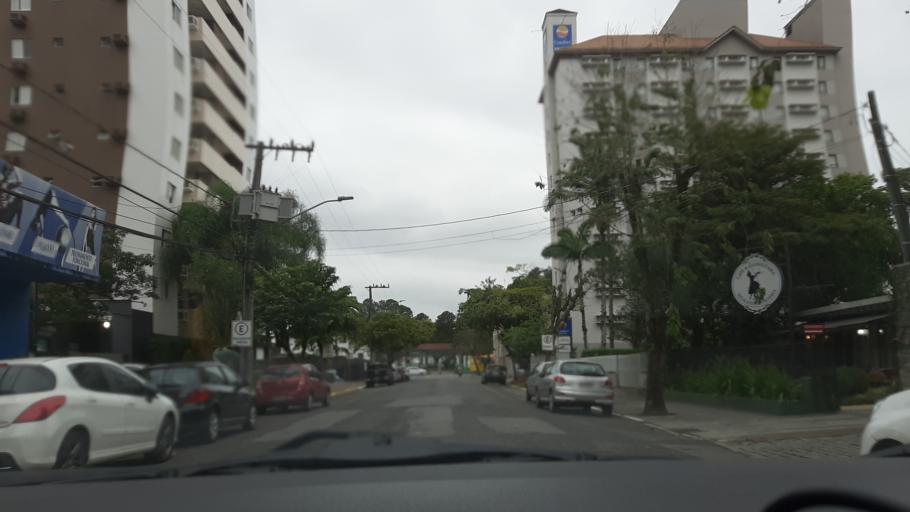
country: BR
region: Santa Catarina
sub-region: Joinville
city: Joinville
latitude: -26.3060
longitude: -48.8507
